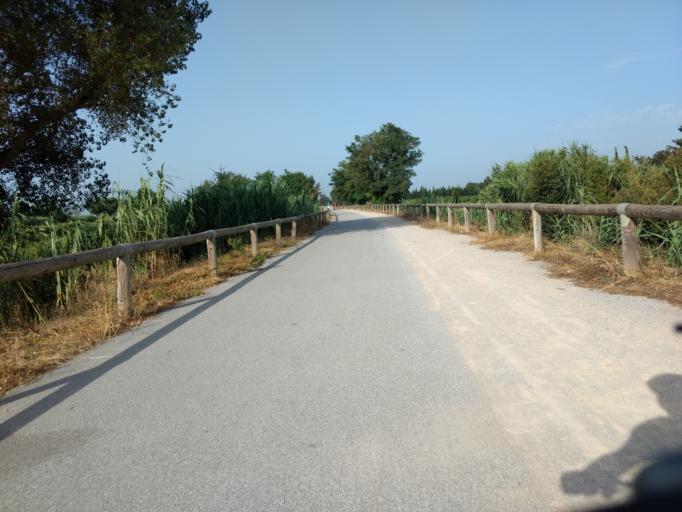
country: FR
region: Languedoc-Roussillon
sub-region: Departement des Pyrenees-Orientales
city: Torreilles
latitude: 42.7607
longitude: 2.9759
